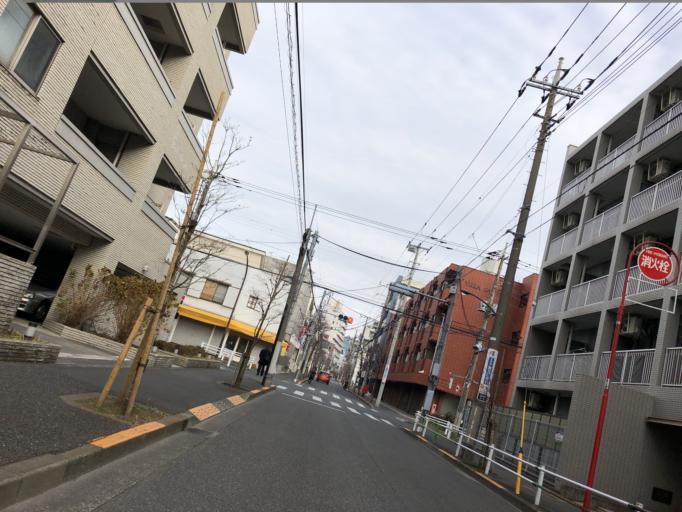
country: JP
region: Tokyo
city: Kamirenjaku
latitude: 35.6975
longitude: 139.5441
